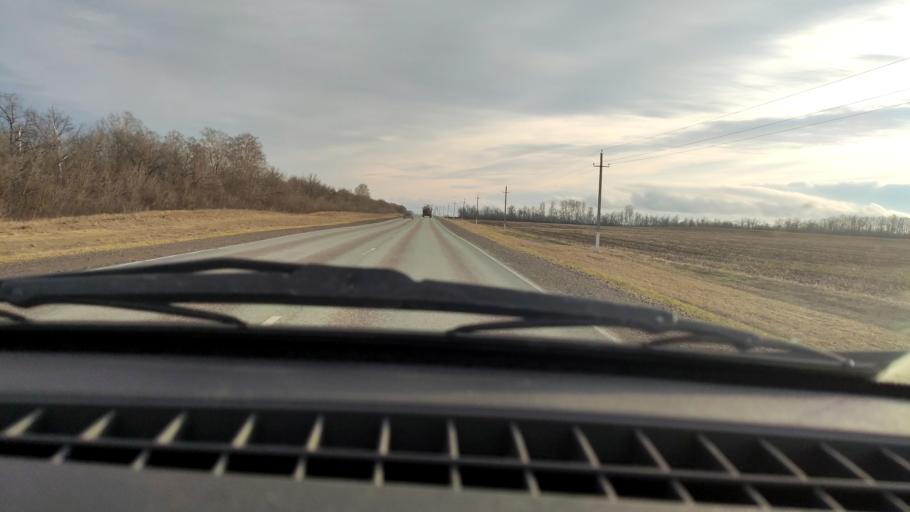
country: RU
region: Bashkortostan
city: Davlekanovo
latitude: 54.3220
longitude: 55.1572
